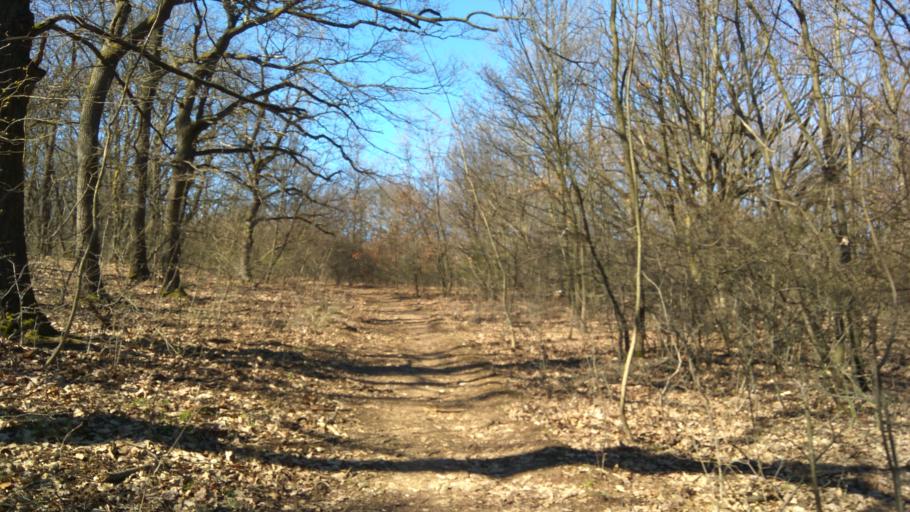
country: HU
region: Pest
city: Csobanka
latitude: 47.6468
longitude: 18.9795
